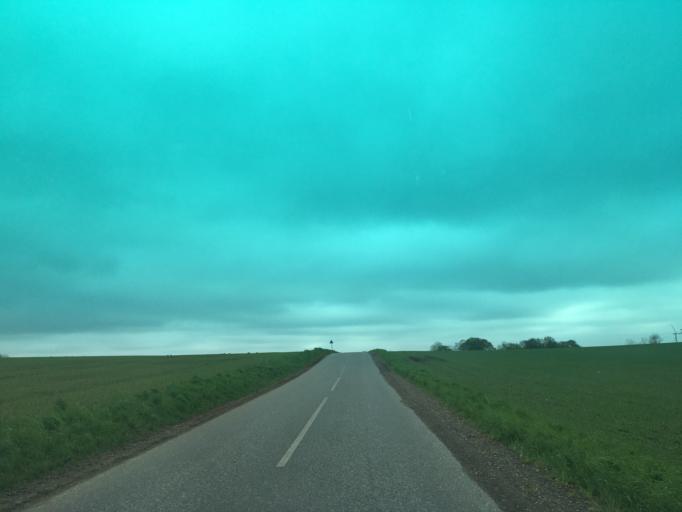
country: DK
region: Zealand
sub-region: Ringsted Kommune
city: Ringsted
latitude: 55.4349
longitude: 11.7164
